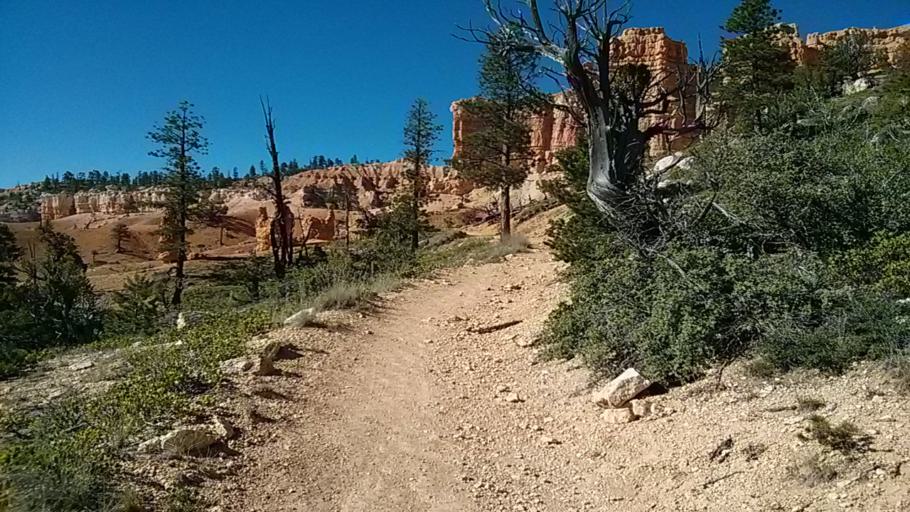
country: US
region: Utah
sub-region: Garfield County
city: Panguitch
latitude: 37.6421
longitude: -112.1347
